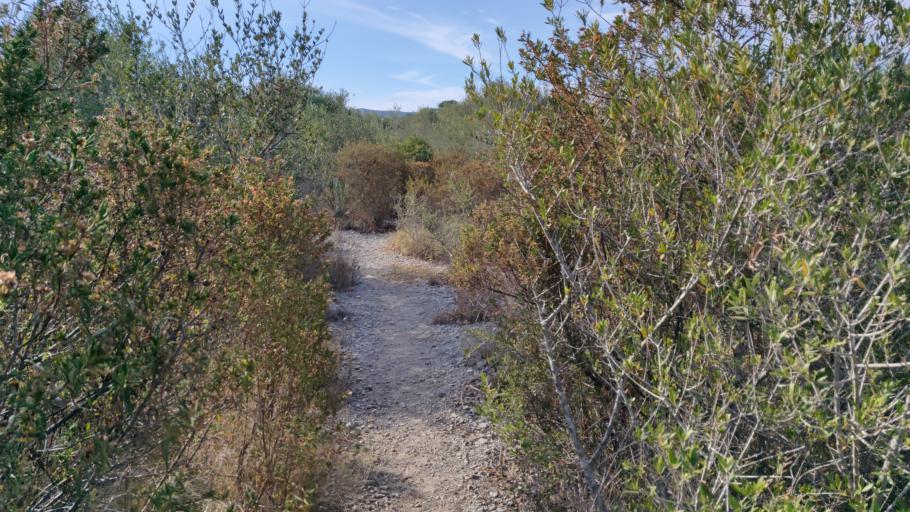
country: ES
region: Balearic Islands
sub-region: Illes Balears
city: Felanitx
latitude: 39.4527
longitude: 3.2624
